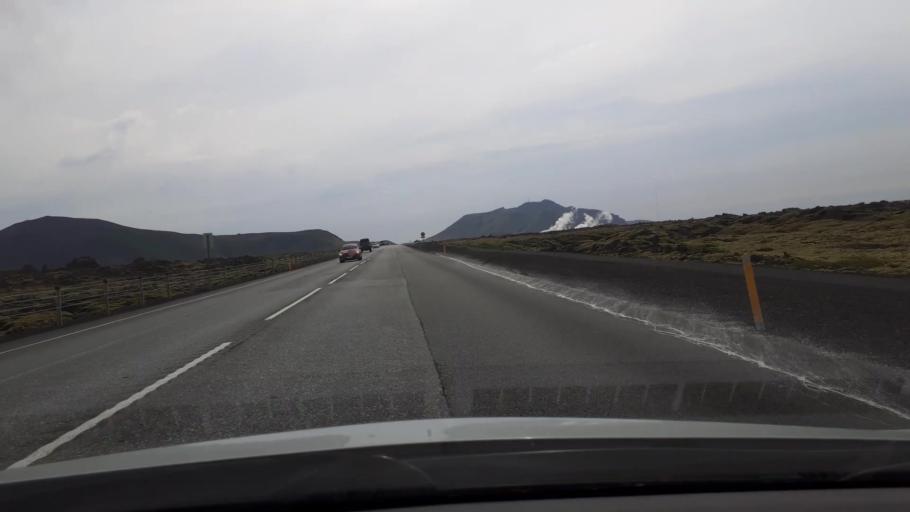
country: IS
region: Southern Peninsula
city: Grindavik
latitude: 63.9010
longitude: -22.4211
